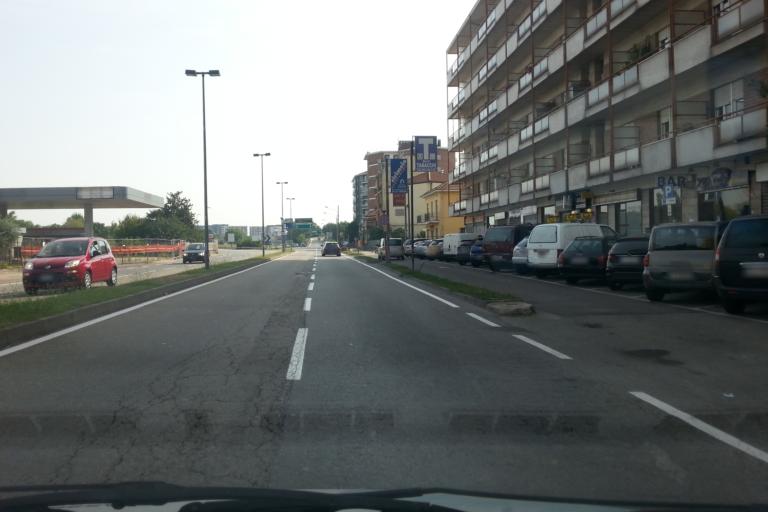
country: IT
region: Piedmont
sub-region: Provincia di Torino
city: Fornaci
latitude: 45.0279
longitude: 7.6002
